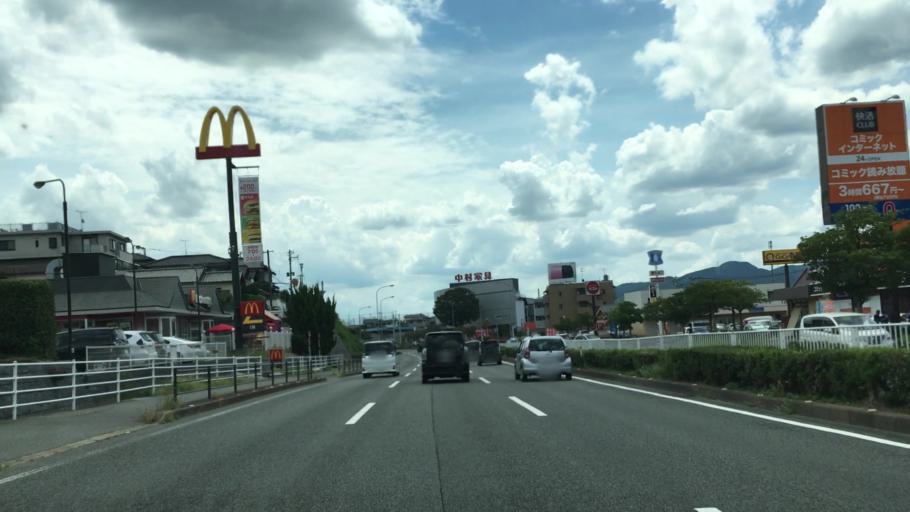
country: JP
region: Fukuoka
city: Dazaifu
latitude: 33.5016
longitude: 130.5314
